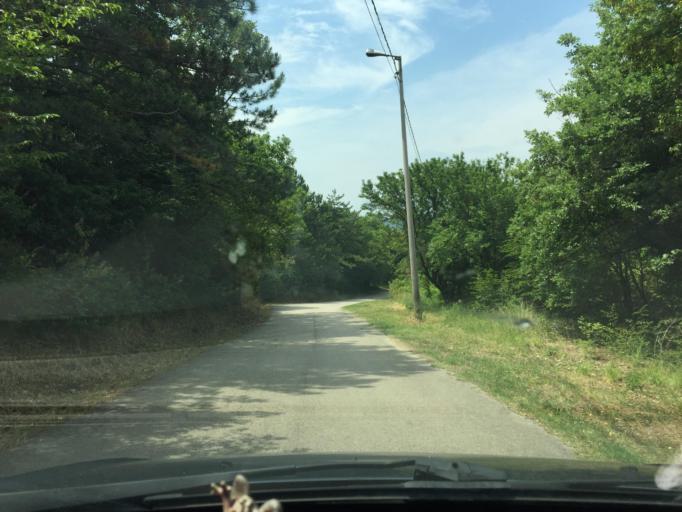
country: IT
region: Friuli Venezia Giulia
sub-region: Provincia di Trieste
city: Domio
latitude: 45.6012
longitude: 13.8136
